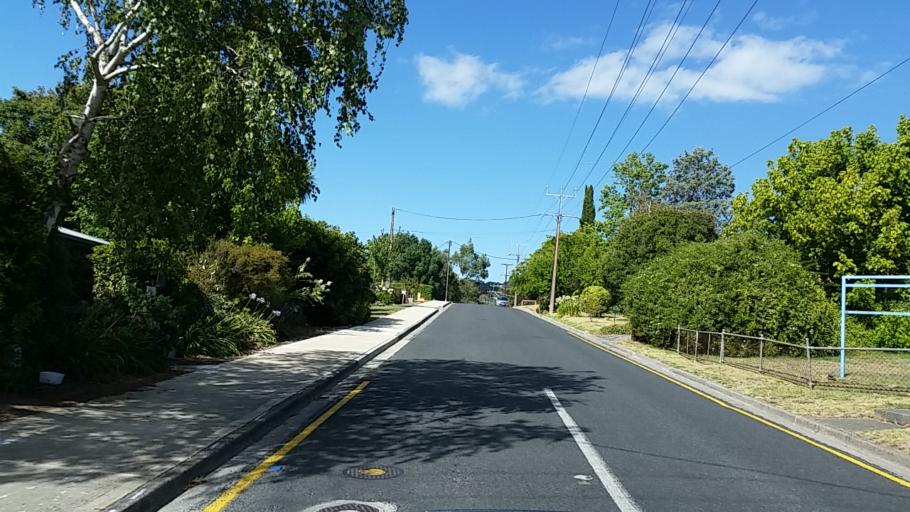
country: AU
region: South Australia
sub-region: Mount Barker
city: Hahndorf
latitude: -35.0313
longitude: 138.8145
